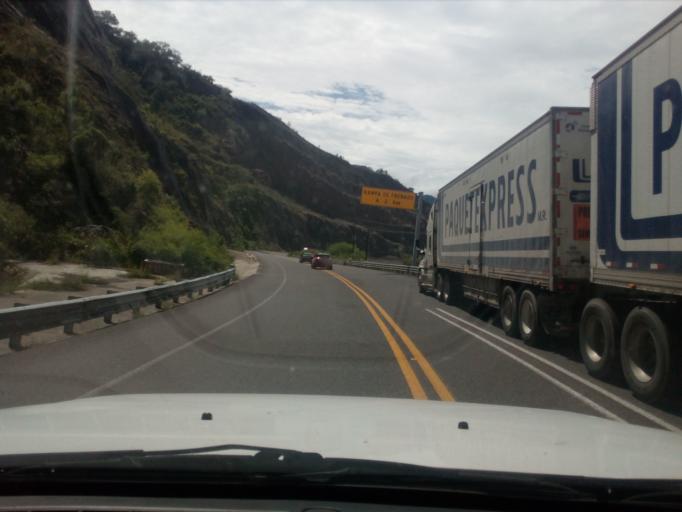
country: MX
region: Durango
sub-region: Pueblo Nuevo
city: La Ciudad
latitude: 23.5633
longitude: -105.7460
